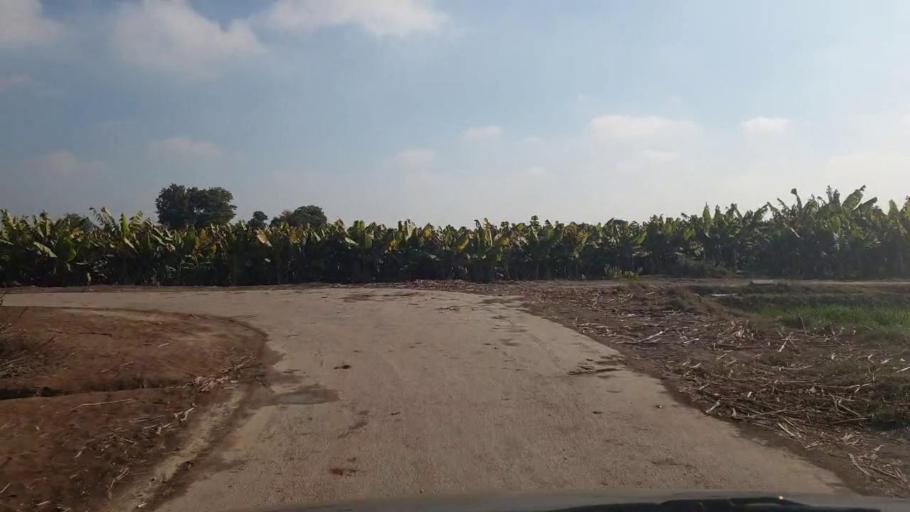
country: PK
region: Sindh
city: Shahdadpur
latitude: 25.8922
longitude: 68.5962
